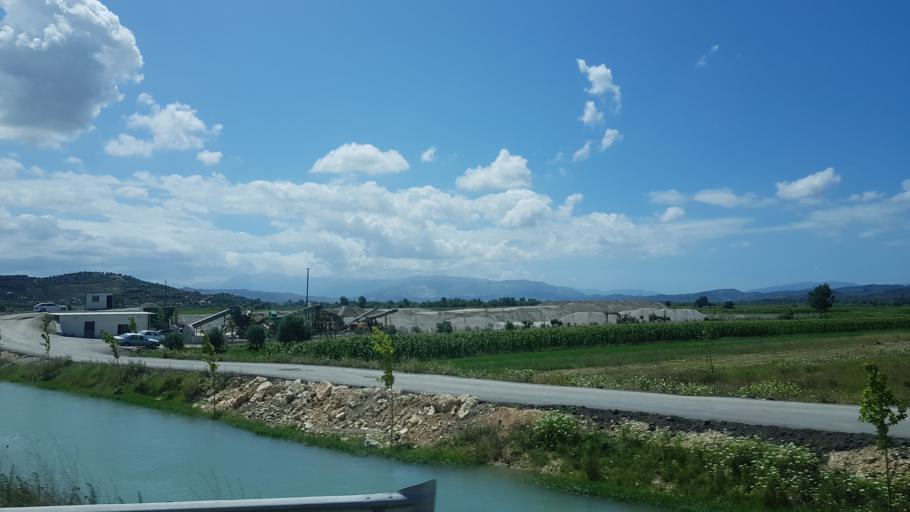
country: AL
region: Fier
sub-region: Rrethi i Fierit
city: Cakran
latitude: 40.5943
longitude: 19.5765
